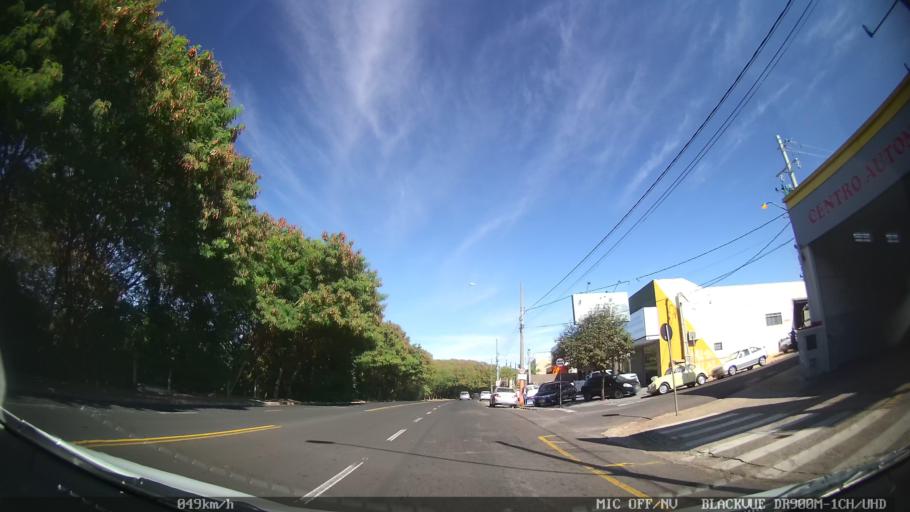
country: BR
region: Sao Paulo
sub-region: Sao Jose Do Rio Preto
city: Sao Jose do Rio Preto
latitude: -20.8001
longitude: -49.4037
